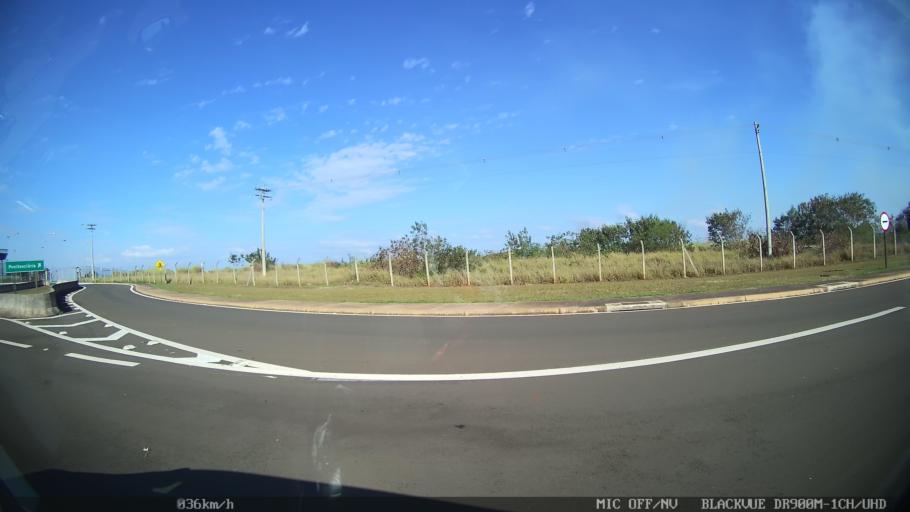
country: BR
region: Sao Paulo
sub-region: Piracicaba
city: Piracicaba
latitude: -22.6793
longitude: -47.5650
